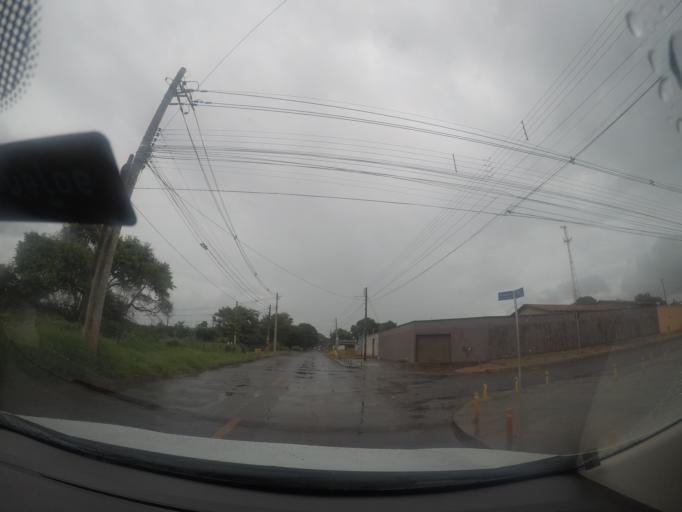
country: BR
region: Goias
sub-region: Trindade
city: Trindade
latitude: -16.6406
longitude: -49.4308
